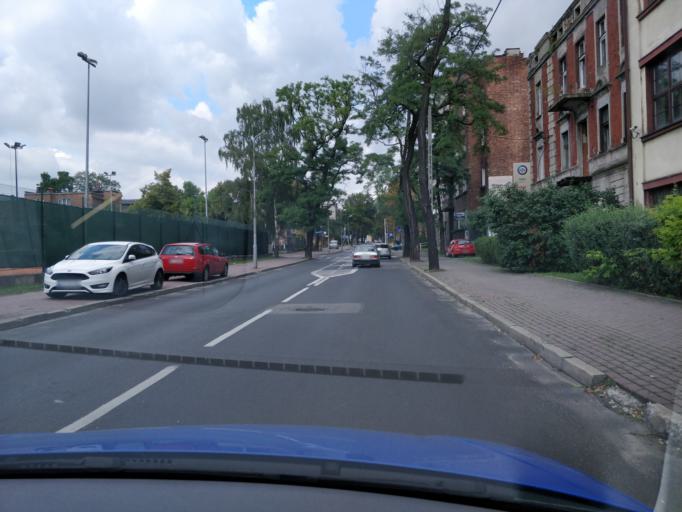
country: PL
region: Silesian Voivodeship
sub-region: Sosnowiec
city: Sosnowiec
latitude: 50.2804
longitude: 19.1177
